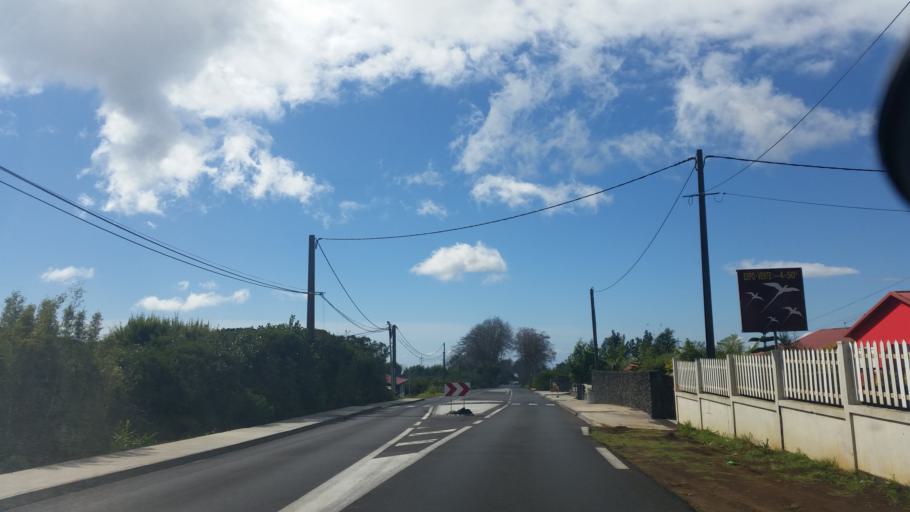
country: RE
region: Reunion
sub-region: Reunion
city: Saint-Benoit
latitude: -21.1220
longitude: 55.6418
